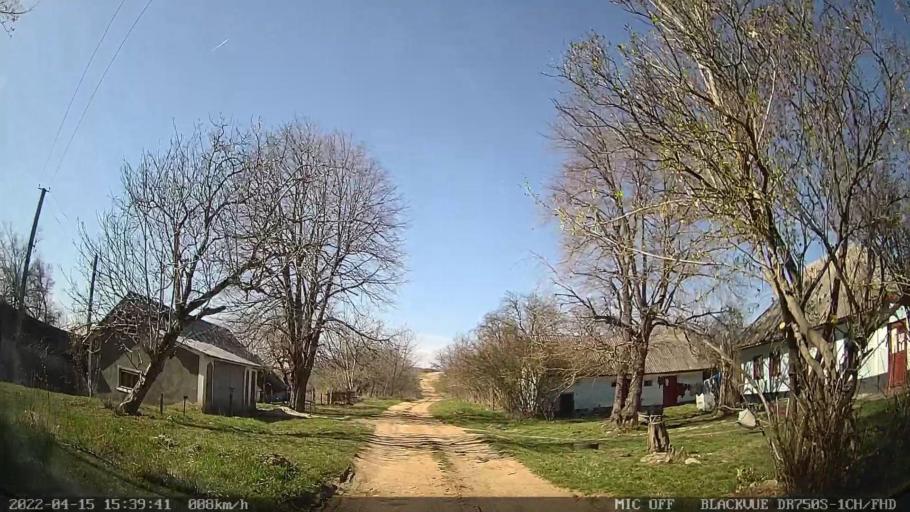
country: MD
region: Raionul Ocnita
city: Otaci
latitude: 48.3539
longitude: 27.9269
